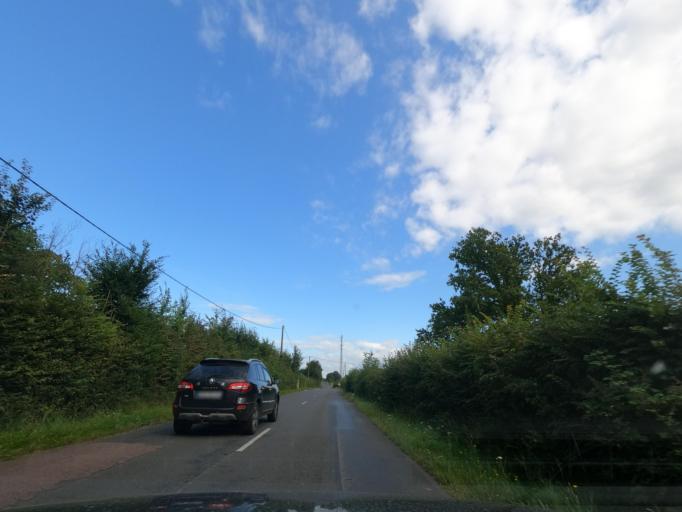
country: FR
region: Lower Normandy
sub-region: Departement de l'Orne
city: Gace
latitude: 48.7587
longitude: 0.1885
